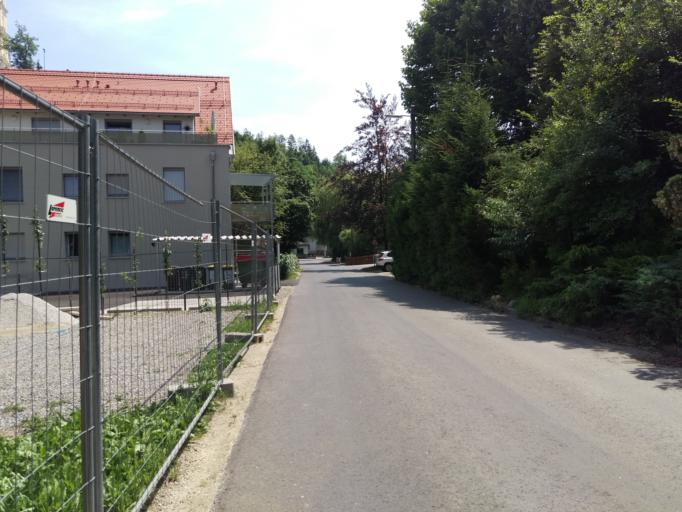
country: AT
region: Styria
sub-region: Graz Stadt
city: Mariatrost
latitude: 47.1087
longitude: 15.4896
